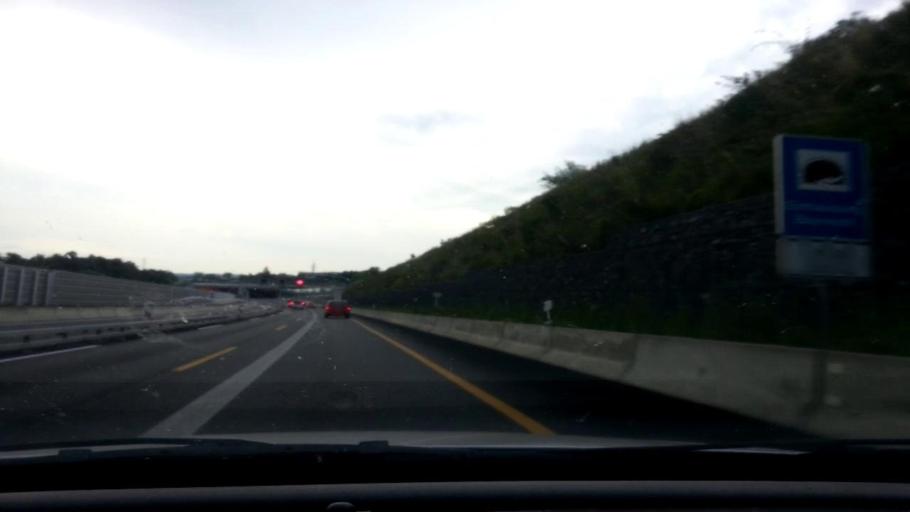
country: DE
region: Bavaria
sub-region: Upper Franconia
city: Bayreuth
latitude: 49.9500
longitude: 11.6078
